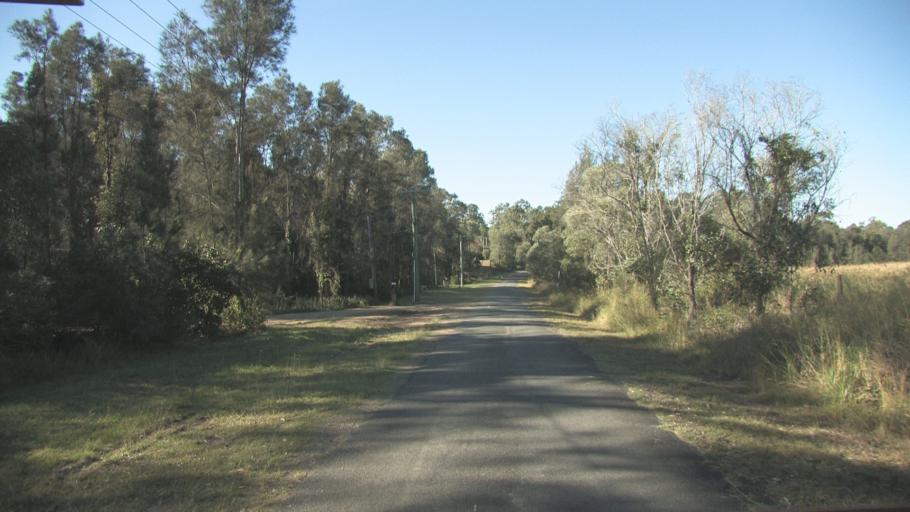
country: AU
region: Queensland
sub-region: Logan
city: Logan Reserve
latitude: -27.7361
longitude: 153.0952
